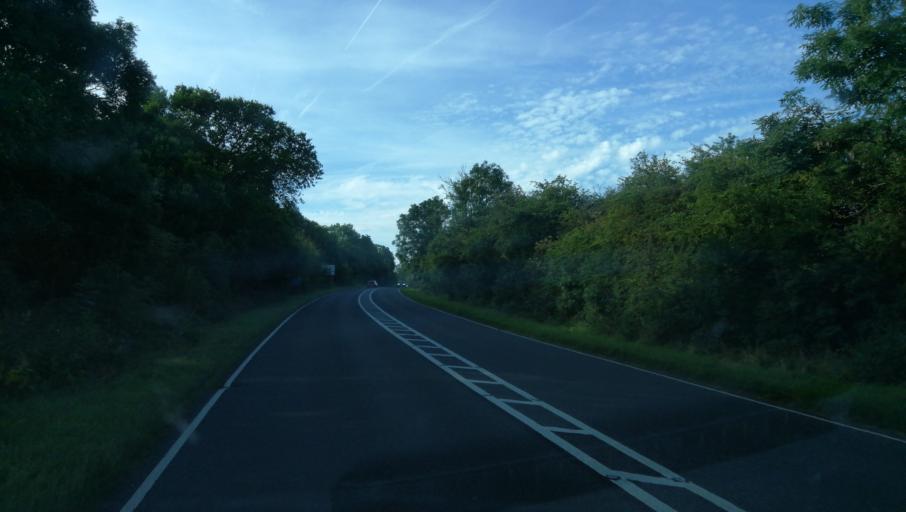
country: GB
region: England
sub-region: Oxfordshire
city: Deddington
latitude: 51.9573
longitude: -1.3181
